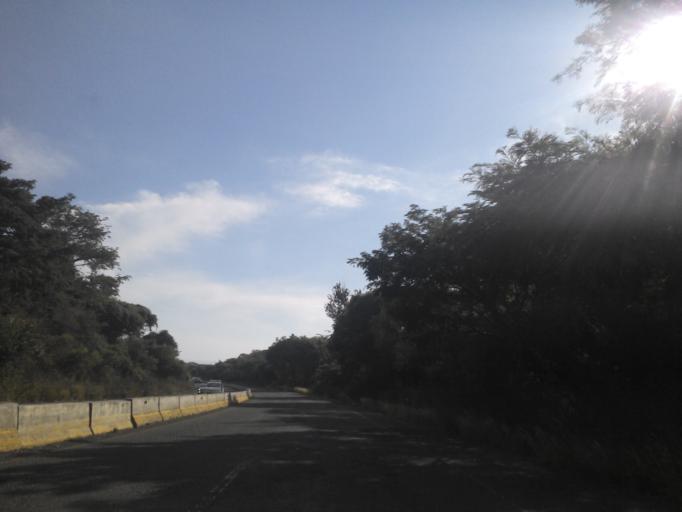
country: MX
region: Jalisco
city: Ixtlahuacan de los Membrillos
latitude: 20.3225
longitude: -103.1979
